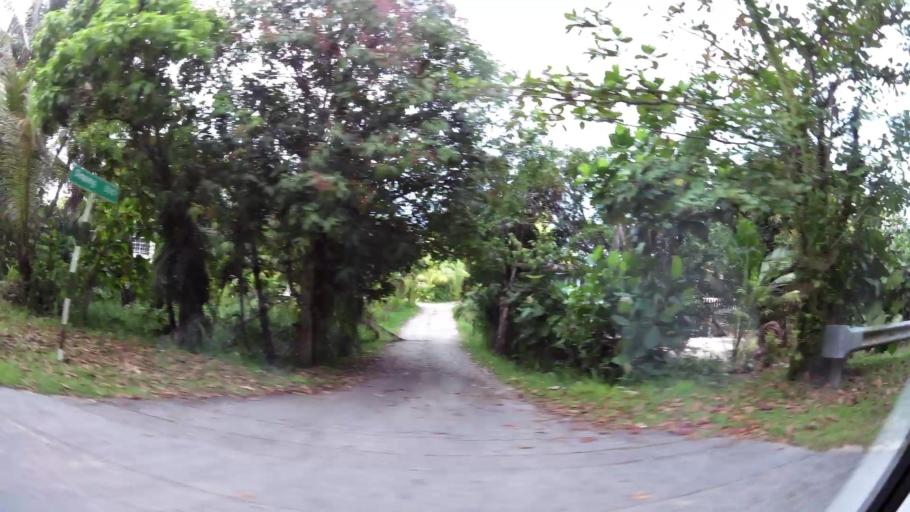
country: BN
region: Brunei and Muara
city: Bandar Seri Begawan
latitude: 4.9398
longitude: 115.0186
